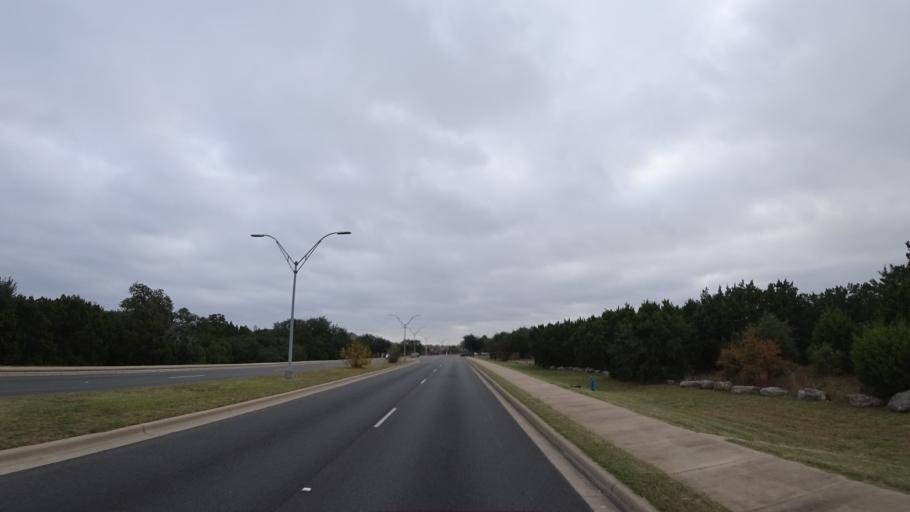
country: US
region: Texas
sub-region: Williamson County
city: Cedar Park
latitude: 30.4982
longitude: -97.8457
